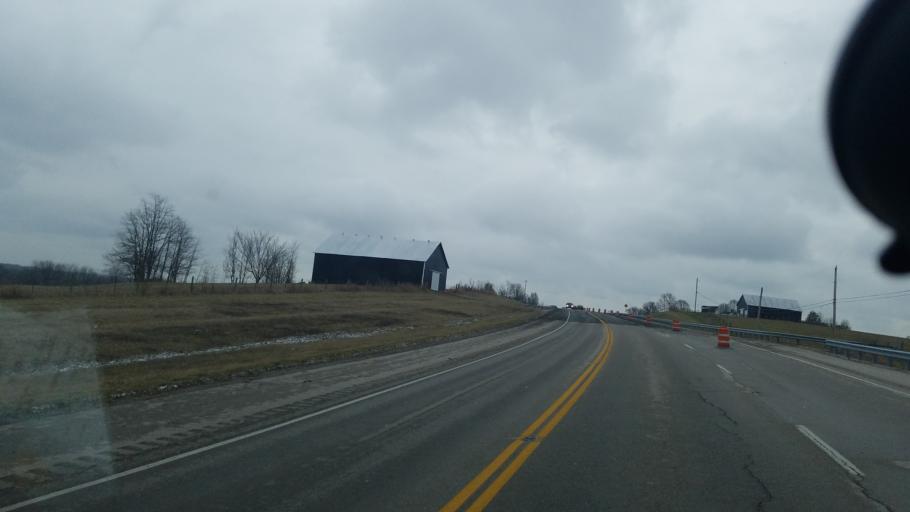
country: US
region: Kentucky
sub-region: Montgomery County
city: Mount Sterling
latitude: 38.1575
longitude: -83.9575
